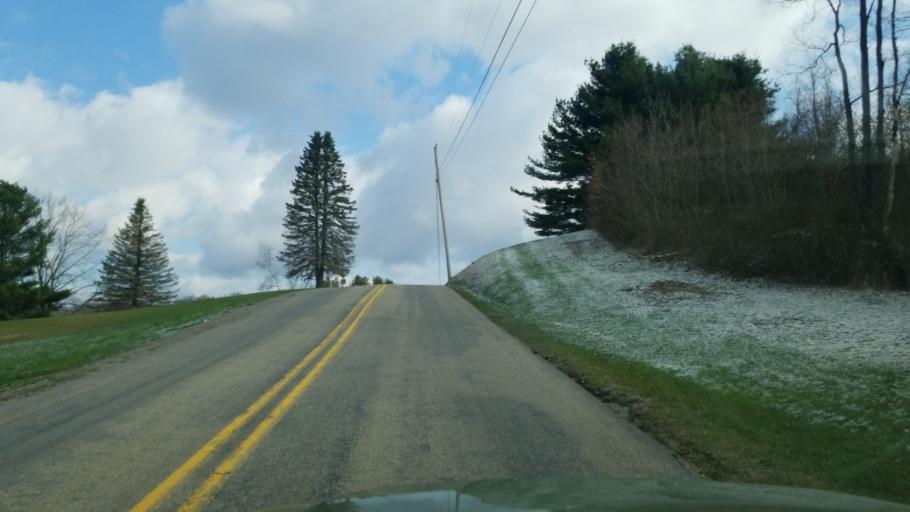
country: US
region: Pennsylvania
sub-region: Jefferson County
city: Brockway
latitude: 41.2635
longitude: -78.8417
